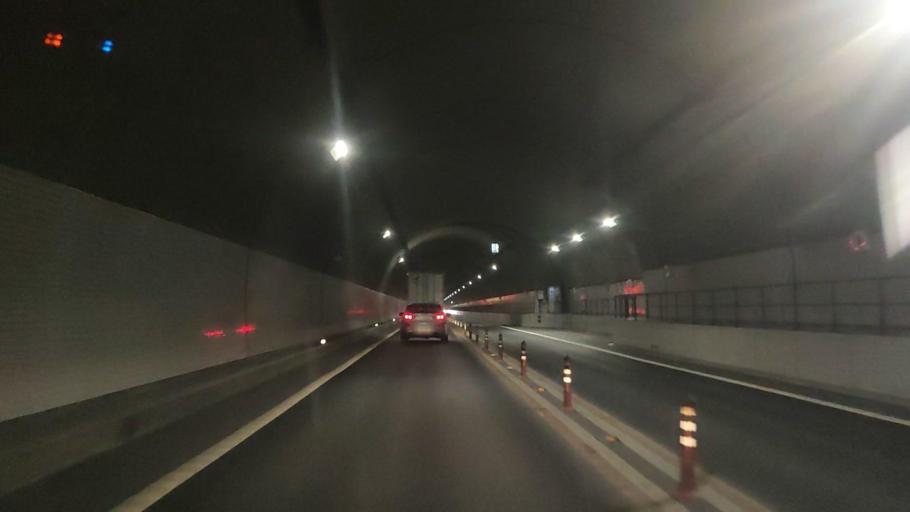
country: JP
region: Fukuoka
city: Kanda
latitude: 33.7606
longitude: 130.9608
